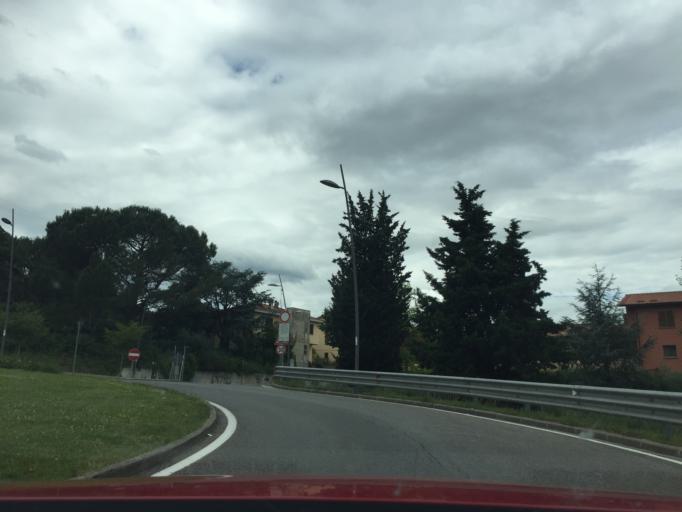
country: IT
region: Tuscany
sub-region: Province of Florence
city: Montelupo Fiorentino
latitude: 43.7271
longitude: 11.0183
